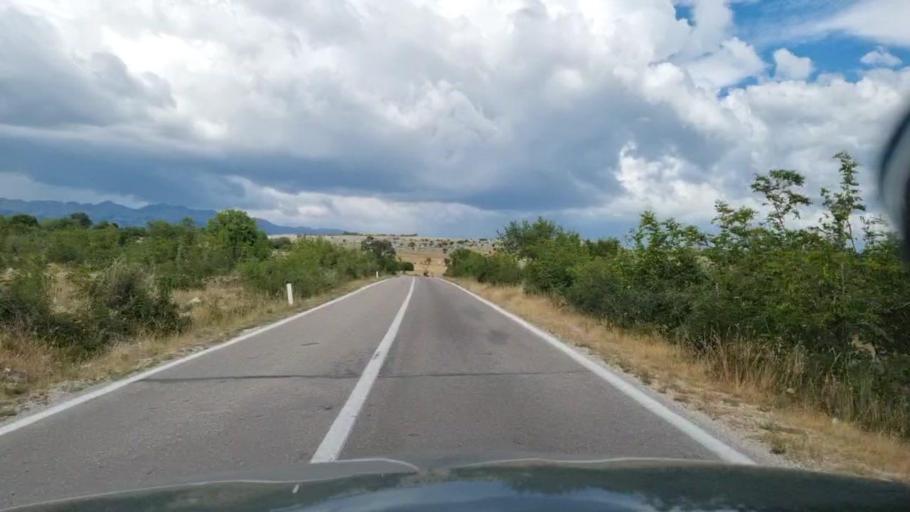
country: BA
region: Federation of Bosnia and Herzegovina
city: Blagaj
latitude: 43.2515
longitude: 17.9419
